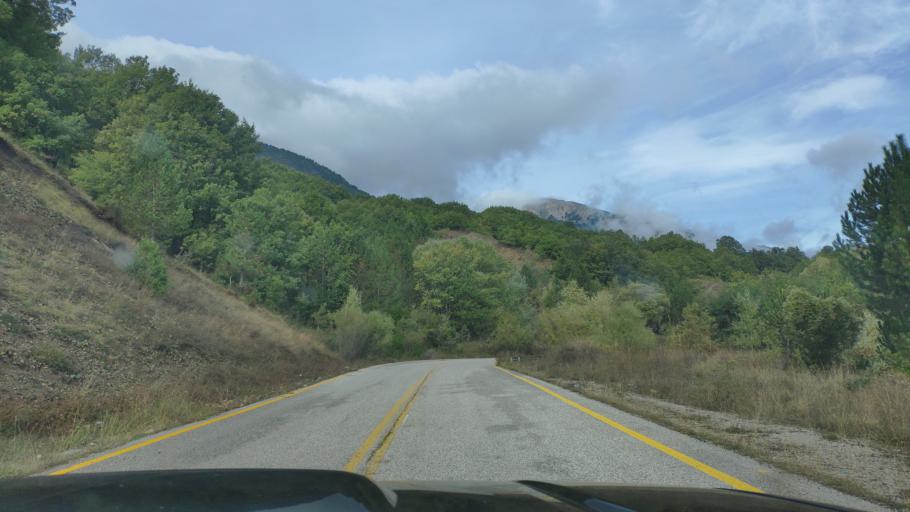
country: GR
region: West Macedonia
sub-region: Nomos Kastorias
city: Nestorio
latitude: 40.2452
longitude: 20.9887
